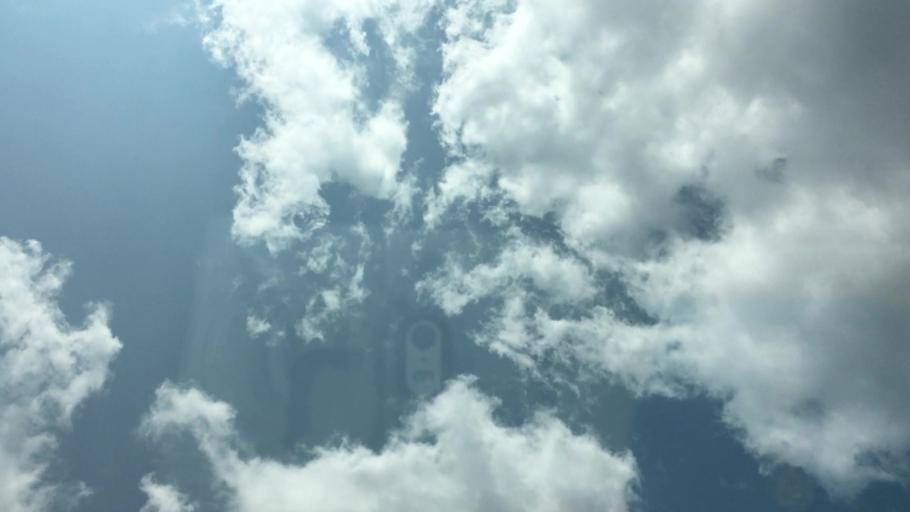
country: US
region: Alabama
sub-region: Pickens County
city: Gordo
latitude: 33.2812
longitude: -87.8000
